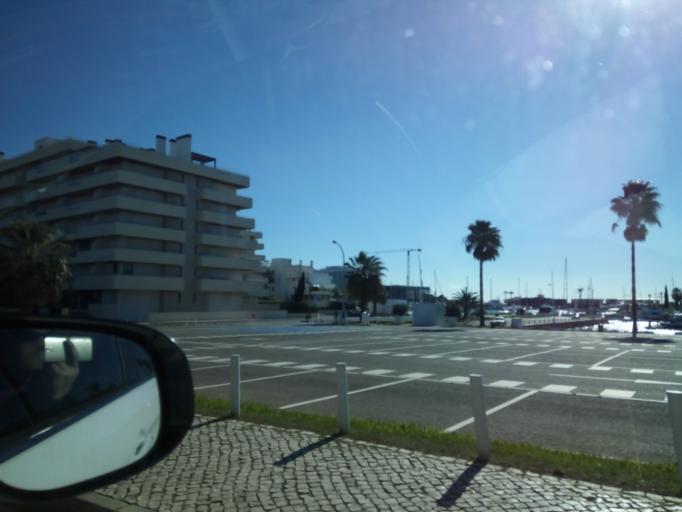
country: PT
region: Faro
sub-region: Loule
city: Vilamoura
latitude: 37.0792
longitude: -8.1243
